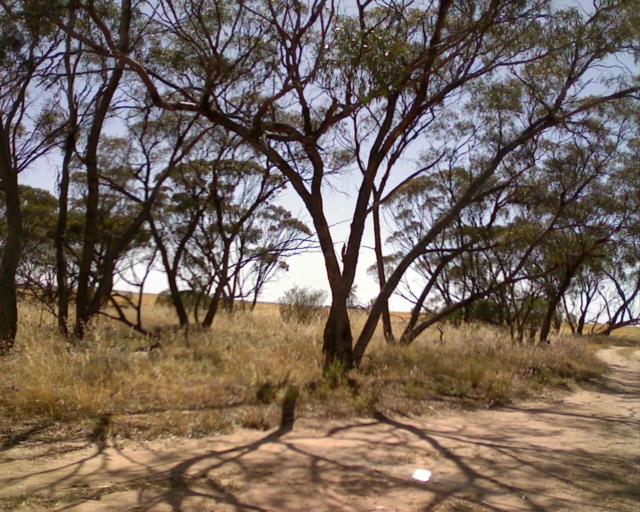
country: AU
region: Western Australia
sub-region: Moora
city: Moora
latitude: -30.0492
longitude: 116.0763
